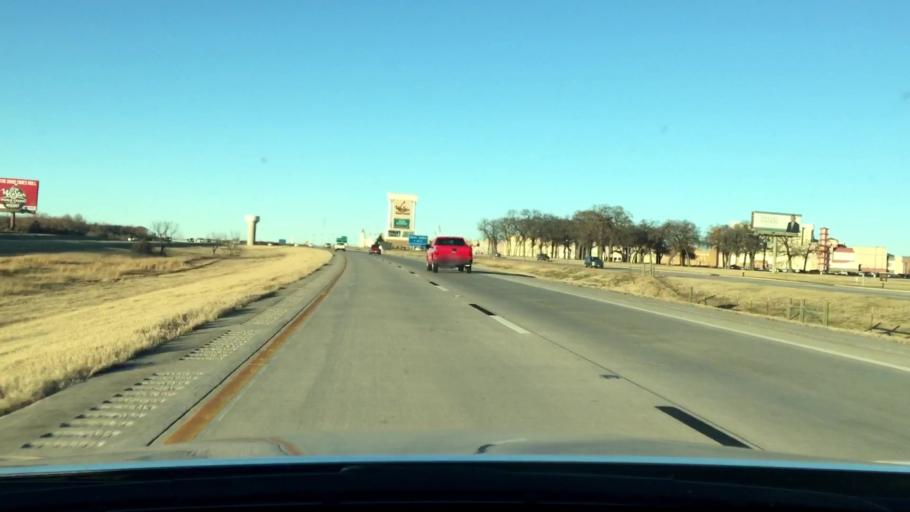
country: US
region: Texas
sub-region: Cooke County
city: Gainesville
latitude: 33.7517
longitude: -97.1354
